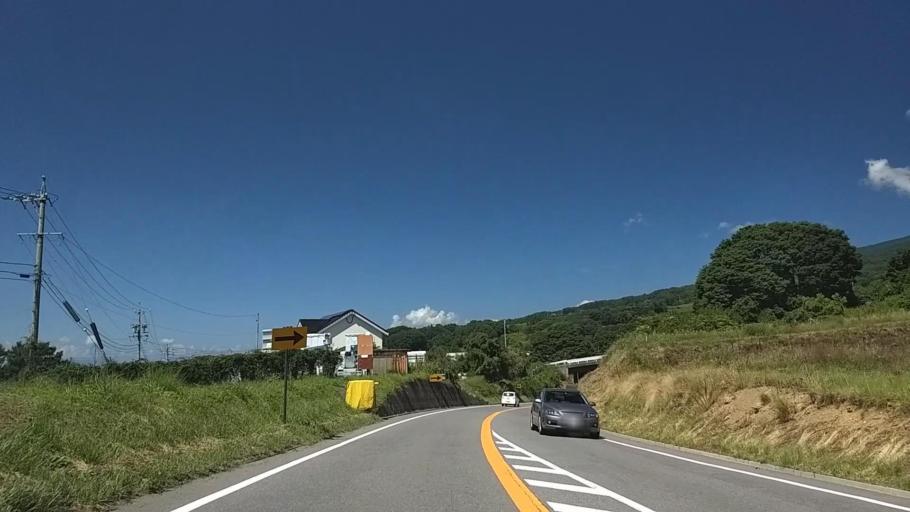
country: JP
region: Nagano
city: Komoro
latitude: 36.3467
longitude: 138.4337
